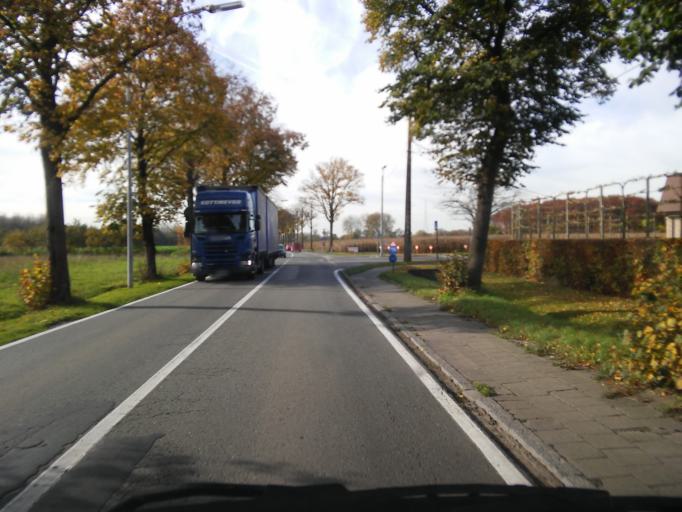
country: BE
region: Flanders
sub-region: Provincie Antwerpen
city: Sint-Amands
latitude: 51.0439
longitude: 4.2403
